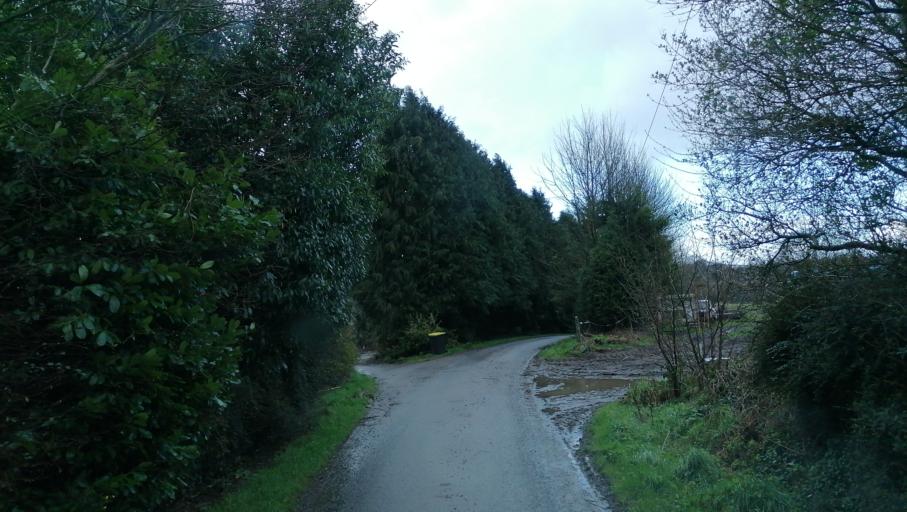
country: FR
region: Brittany
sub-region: Departement des Cotes-d'Armor
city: Lanrodec
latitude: 48.4893
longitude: -3.0023
